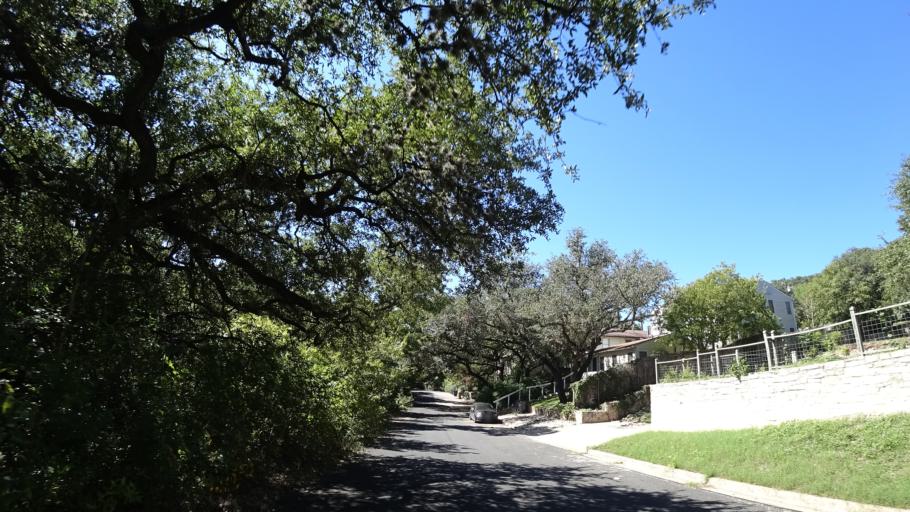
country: US
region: Texas
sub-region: Travis County
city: Austin
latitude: 30.2454
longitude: -97.7398
